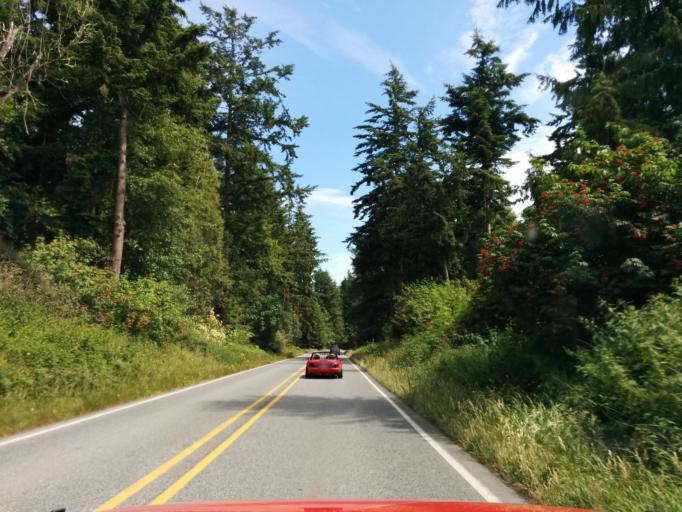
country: US
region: Washington
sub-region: Island County
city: Coupeville
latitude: 48.1818
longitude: -122.6237
